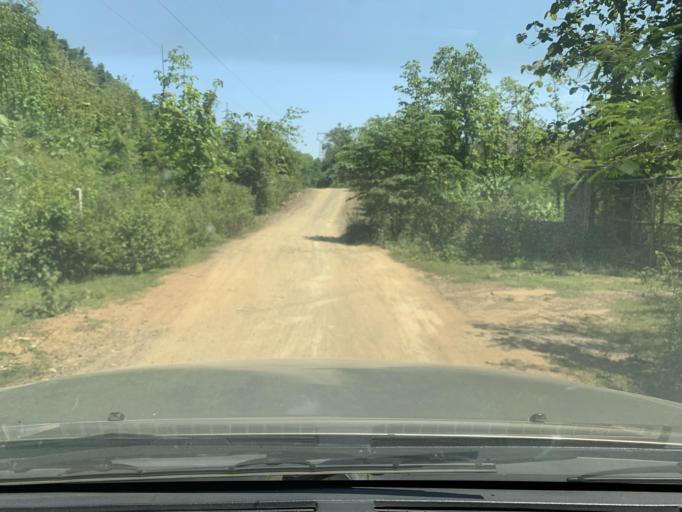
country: LA
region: Louangphabang
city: Louangphabang
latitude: 19.9004
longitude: 102.2168
